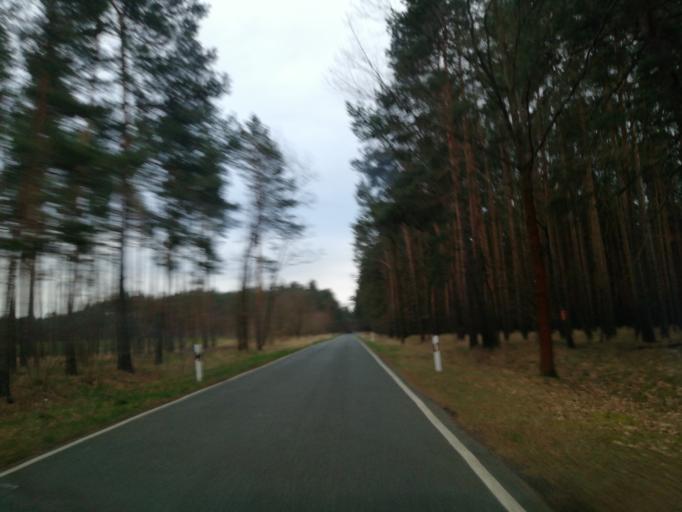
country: DE
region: Brandenburg
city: Vetschau
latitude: 51.7496
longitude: 14.1321
